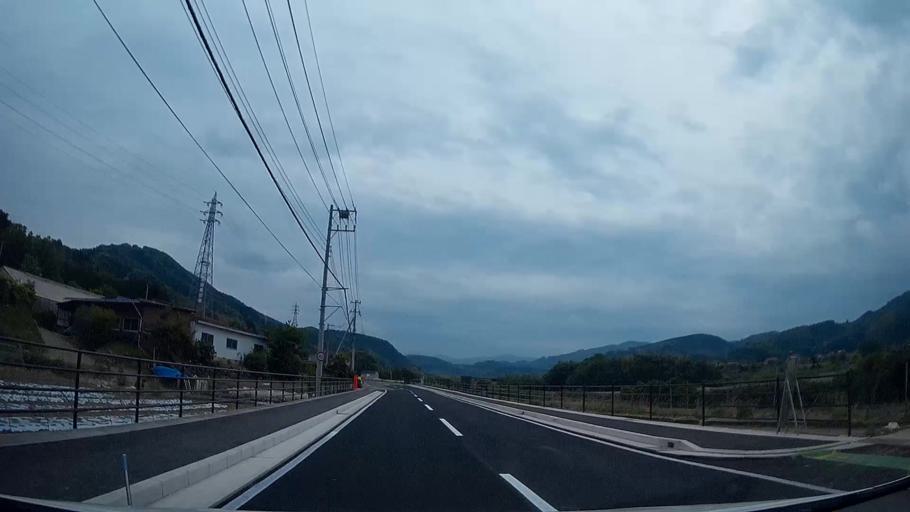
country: JP
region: Shizuoka
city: Ito
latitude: 34.9555
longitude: 138.9434
